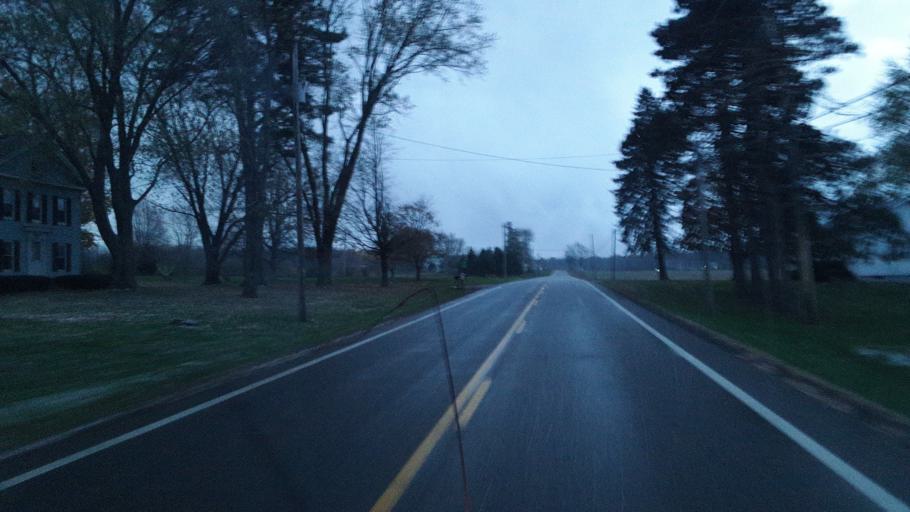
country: US
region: Ohio
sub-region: Portage County
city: Mantua
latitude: 41.3568
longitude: -81.2235
